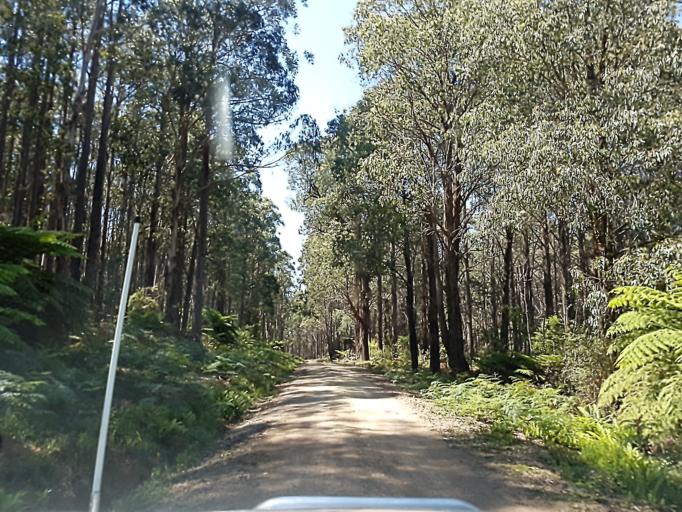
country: AU
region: Victoria
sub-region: East Gippsland
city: Lakes Entrance
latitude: -37.2947
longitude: 148.3147
